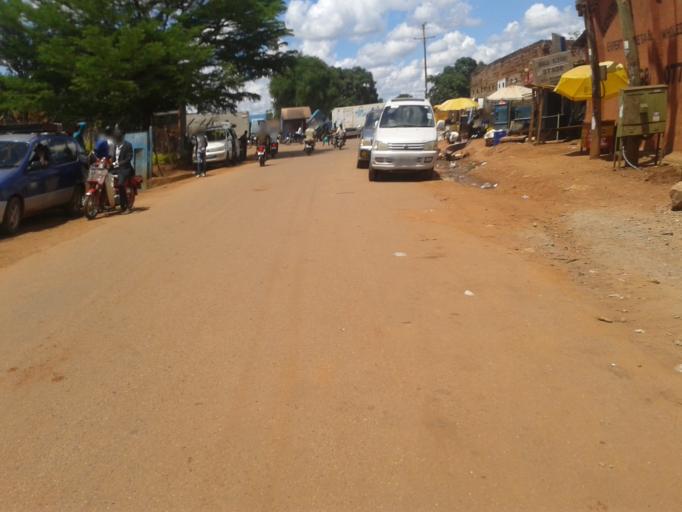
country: UG
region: Northern Region
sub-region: Gulu District
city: Gulu
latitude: 2.7674
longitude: 32.2979
